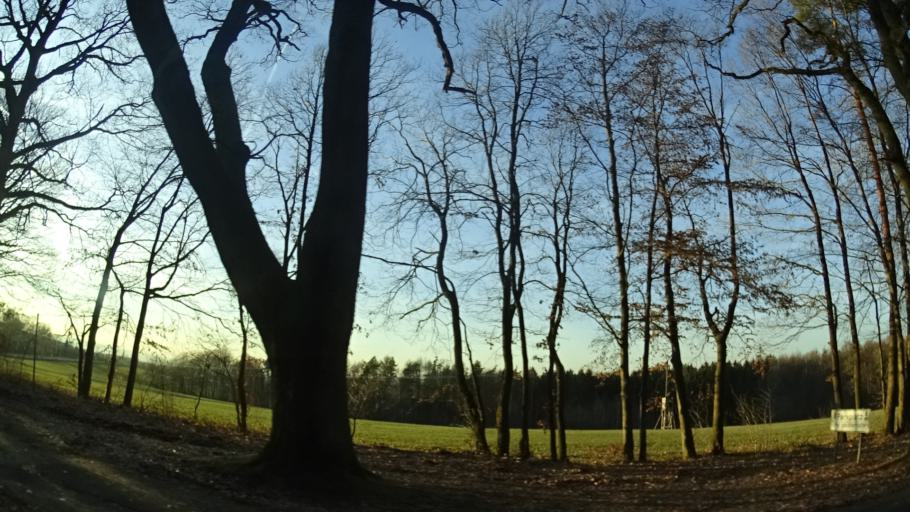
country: DE
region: Bavaria
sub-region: Regierungsbezirk Unterfranken
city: Geiselbach
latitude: 50.1482
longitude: 9.2133
